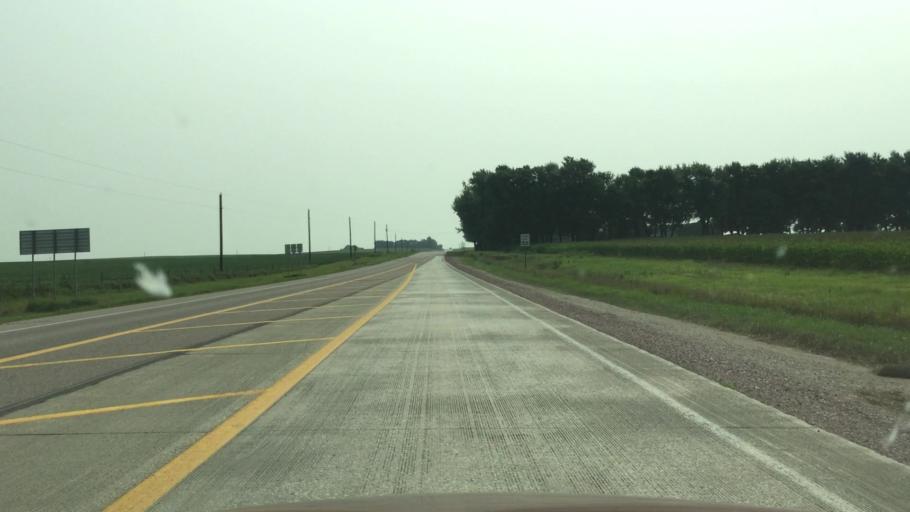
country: US
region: Iowa
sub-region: Osceola County
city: Sibley
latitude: 43.4327
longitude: -95.7113
